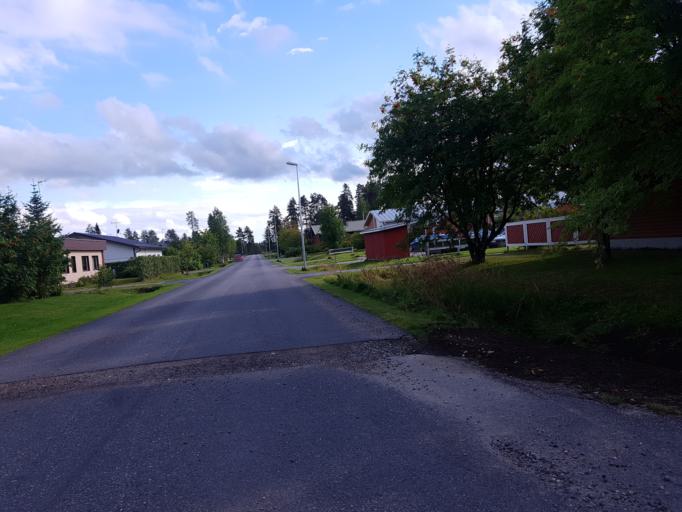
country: FI
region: Kainuu
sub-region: Kehys-Kainuu
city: Kuhmo
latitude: 64.1207
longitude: 29.5348
